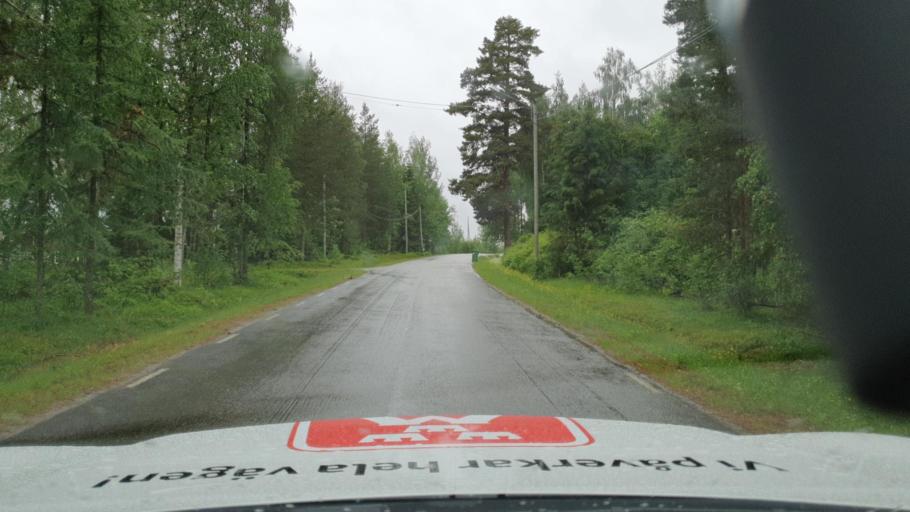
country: SE
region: Vaesterbotten
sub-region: Lycksele Kommun
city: Lycksele
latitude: 64.0768
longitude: 18.3566
